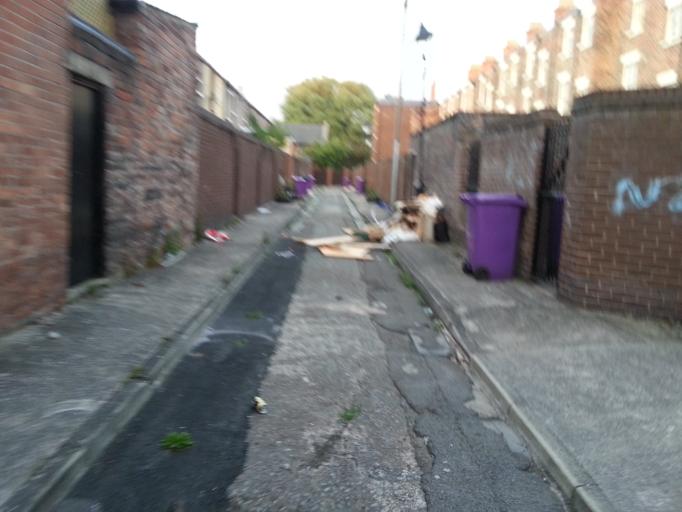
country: GB
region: England
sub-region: Liverpool
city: Liverpool
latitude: 53.3965
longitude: -2.9672
